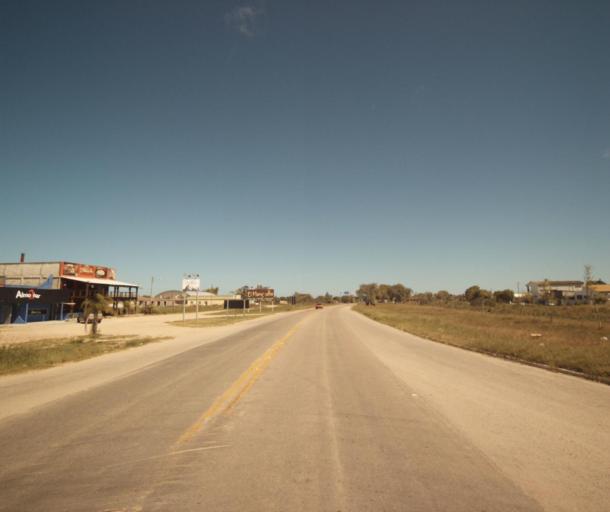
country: BR
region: Rio Grande do Sul
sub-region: Chui
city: Chui
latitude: -33.6898
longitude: -53.4472
